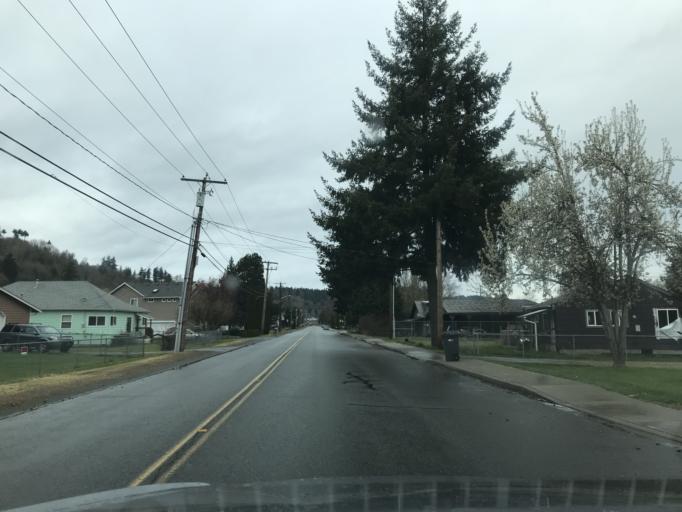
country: US
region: Washington
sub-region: King County
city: Algona
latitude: 47.2828
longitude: -122.2534
